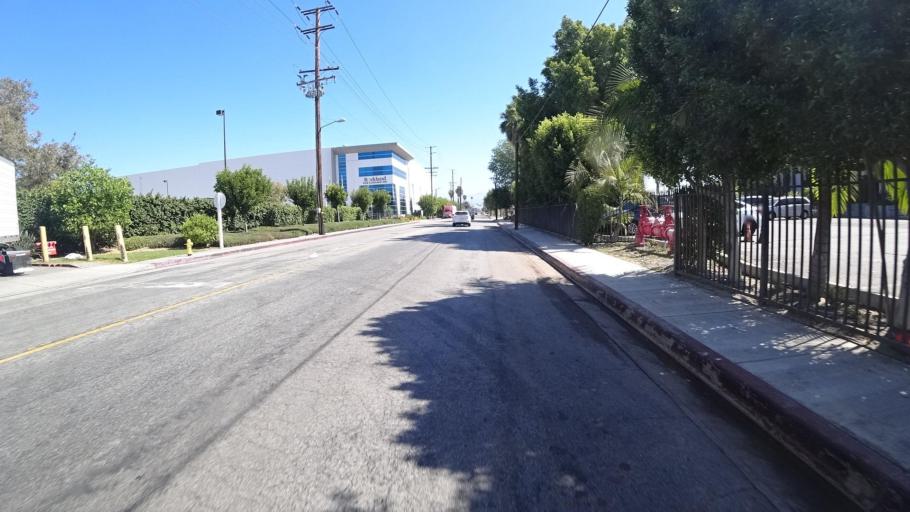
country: US
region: California
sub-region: Los Angeles County
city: Avocado Heights
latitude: 34.0389
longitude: -117.9783
